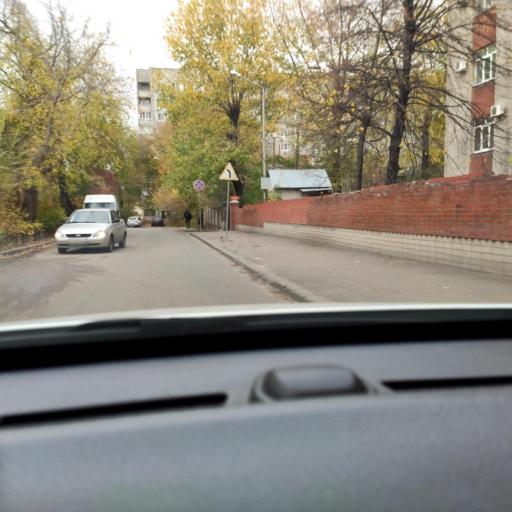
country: RU
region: Voronezj
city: Voronezh
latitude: 51.6956
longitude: 39.2050
